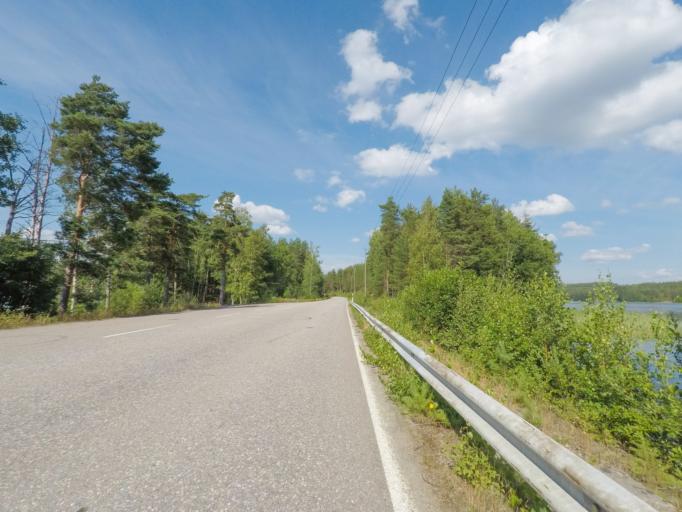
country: FI
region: Southern Savonia
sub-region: Mikkeli
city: Puumala
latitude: 61.4915
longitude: 28.1672
